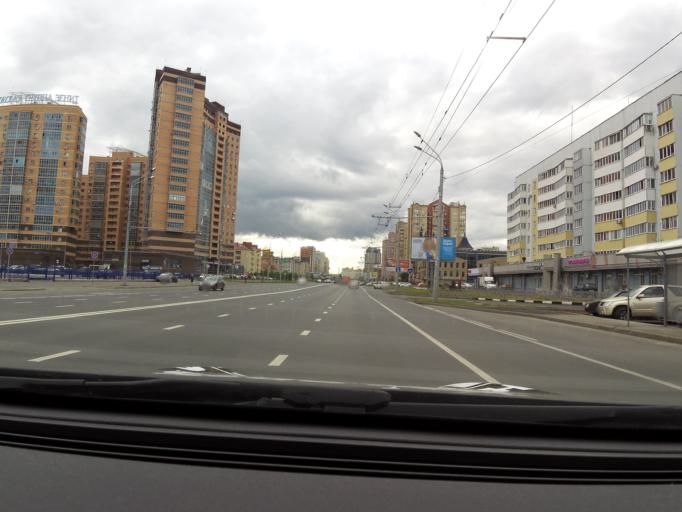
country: RU
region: Tatarstan
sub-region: Gorod Kazan'
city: Kazan
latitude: 55.8195
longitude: 49.1253
